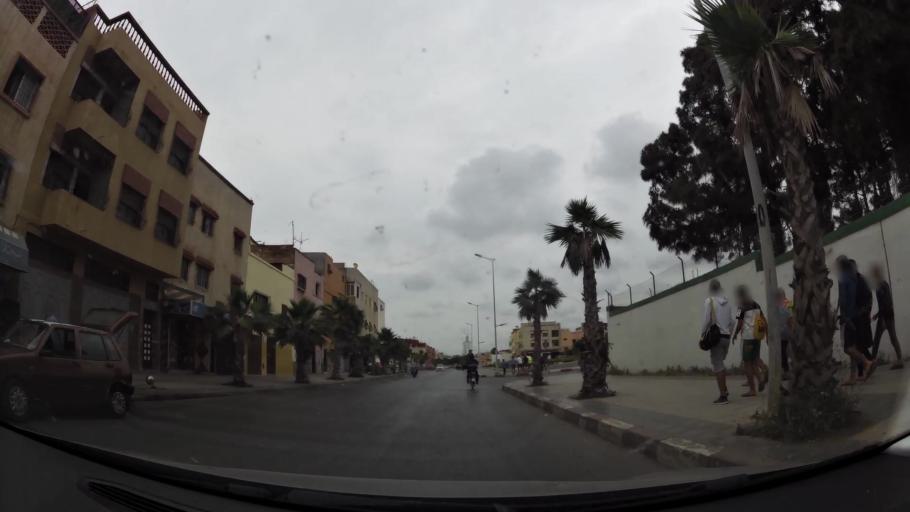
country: MA
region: Rabat-Sale-Zemmour-Zaer
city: Sale
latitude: 34.0439
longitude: -6.7997
